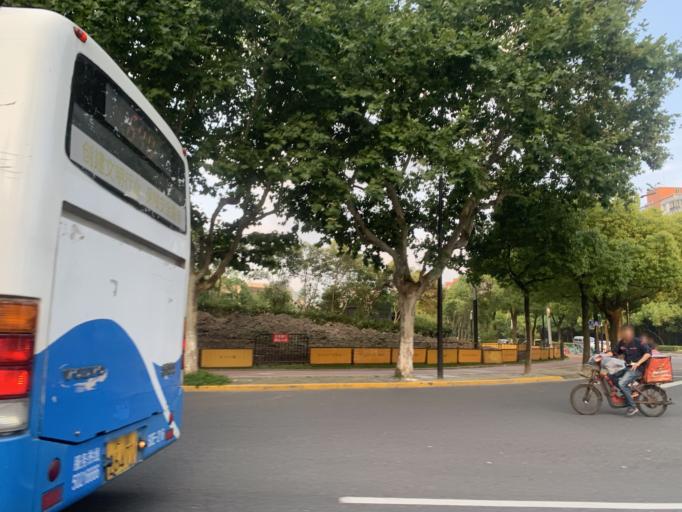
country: CN
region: Shanghai Shi
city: Huamu
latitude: 31.2148
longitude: 121.5377
